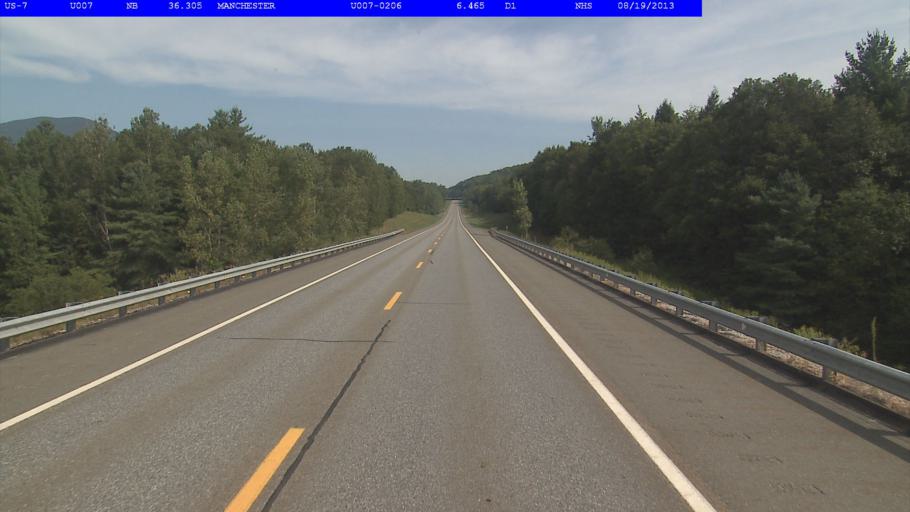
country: US
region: Vermont
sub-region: Bennington County
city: Manchester Center
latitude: 43.1956
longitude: -73.0130
